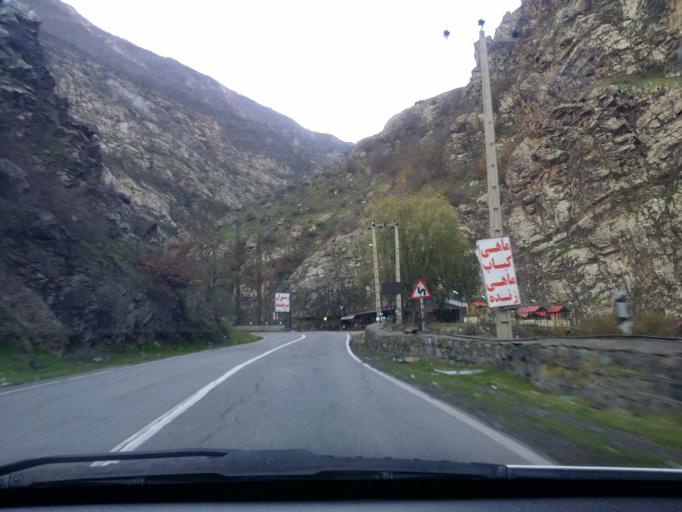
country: IR
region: Mazandaran
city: Chalus
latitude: 36.3025
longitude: 51.2469
